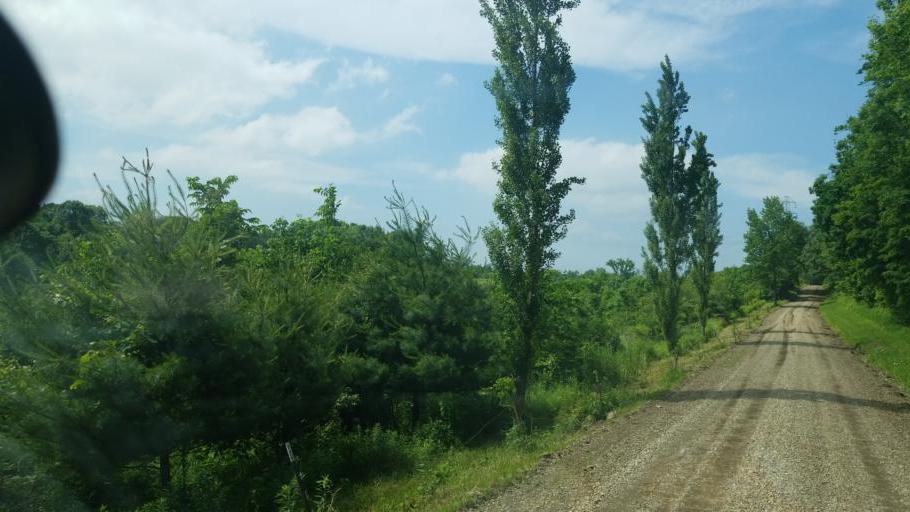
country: US
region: Ohio
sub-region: Muskingum County
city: Frazeysburg
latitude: 40.2606
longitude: -82.1848
